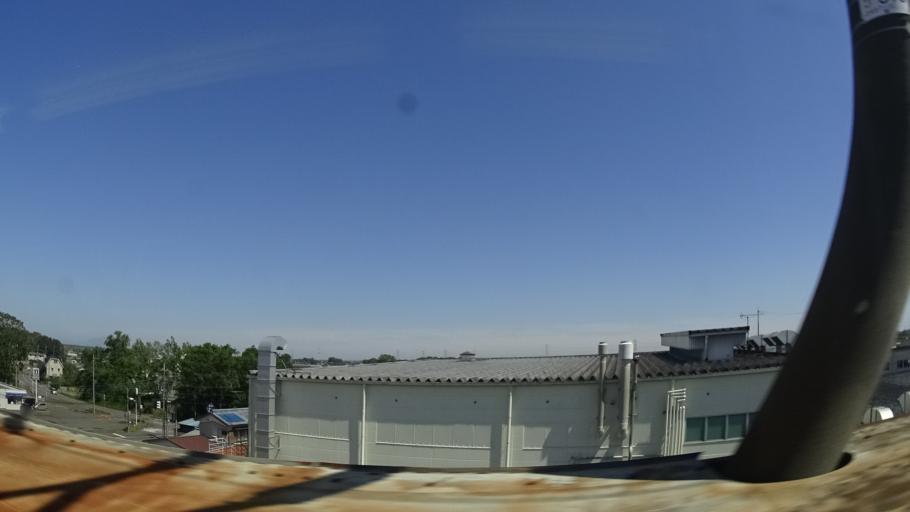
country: JP
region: Saitama
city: Kurihashi
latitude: 36.1275
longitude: 139.7164
